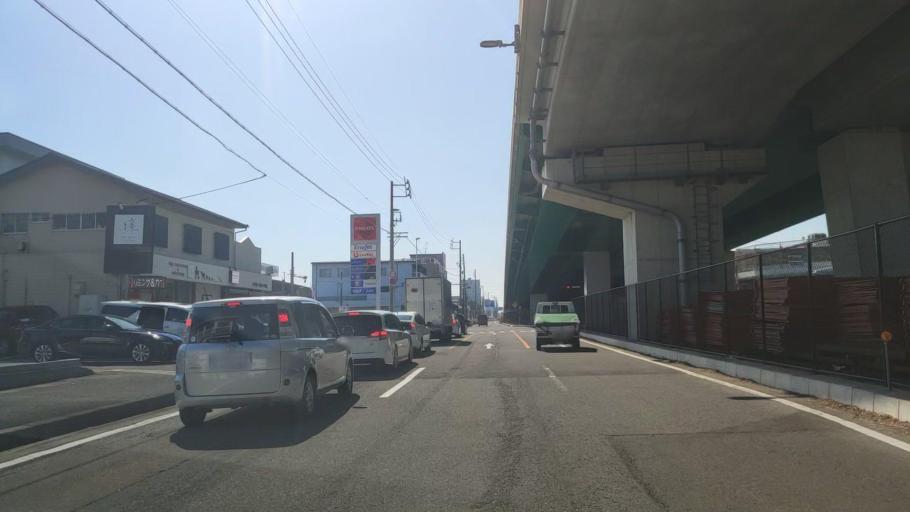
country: JP
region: Gifu
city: Gifu-shi
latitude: 35.4151
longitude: 136.7854
